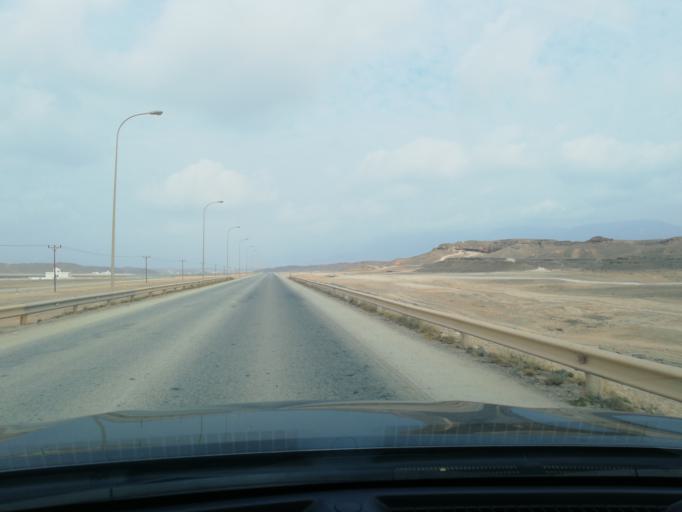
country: OM
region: Zufar
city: Salalah
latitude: 16.9577
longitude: 53.9031
